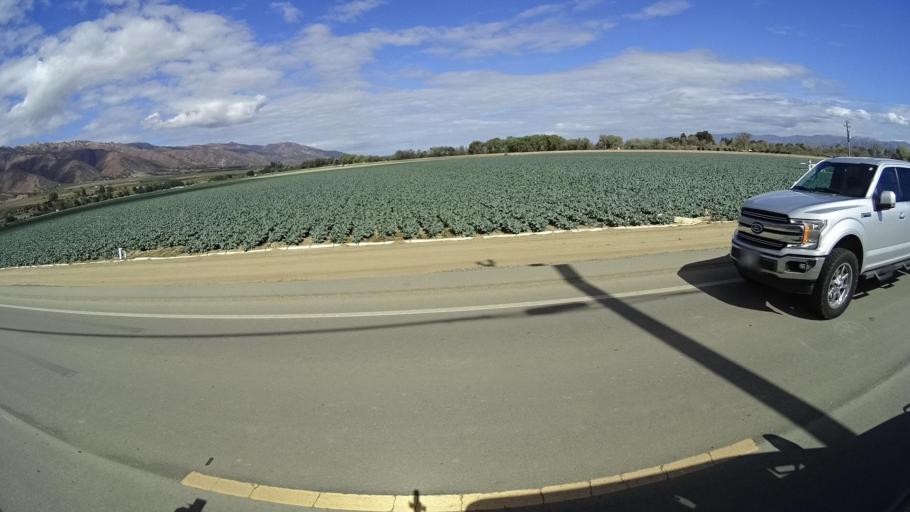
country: US
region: California
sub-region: Monterey County
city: Gonzales
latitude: 36.4813
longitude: -121.4725
